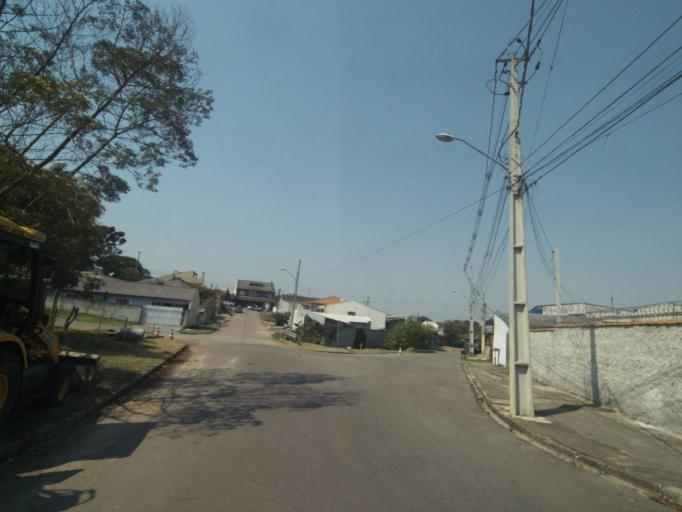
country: BR
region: Parana
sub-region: Sao Jose Dos Pinhais
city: Sao Jose dos Pinhais
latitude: -25.5050
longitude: -49.2682
